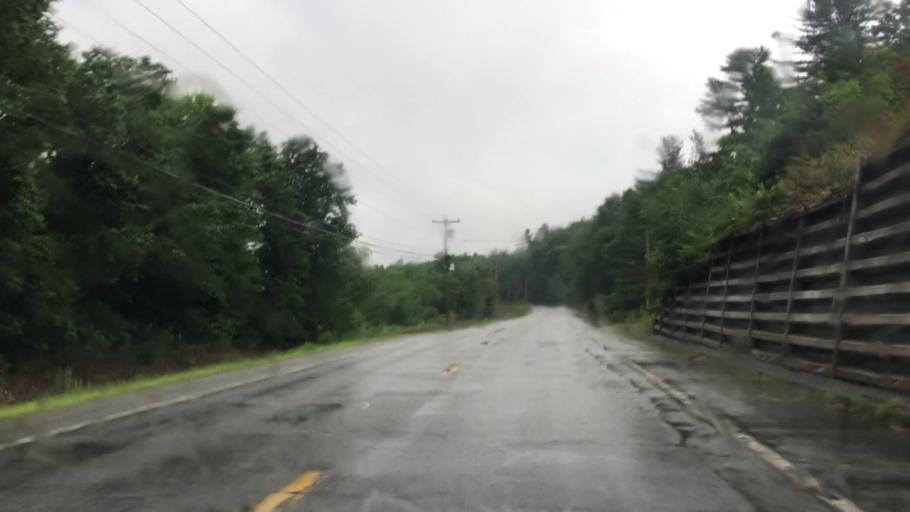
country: US
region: Maine
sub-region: Kennebec County
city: Pittston
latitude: 44.2090
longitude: -69.7641
